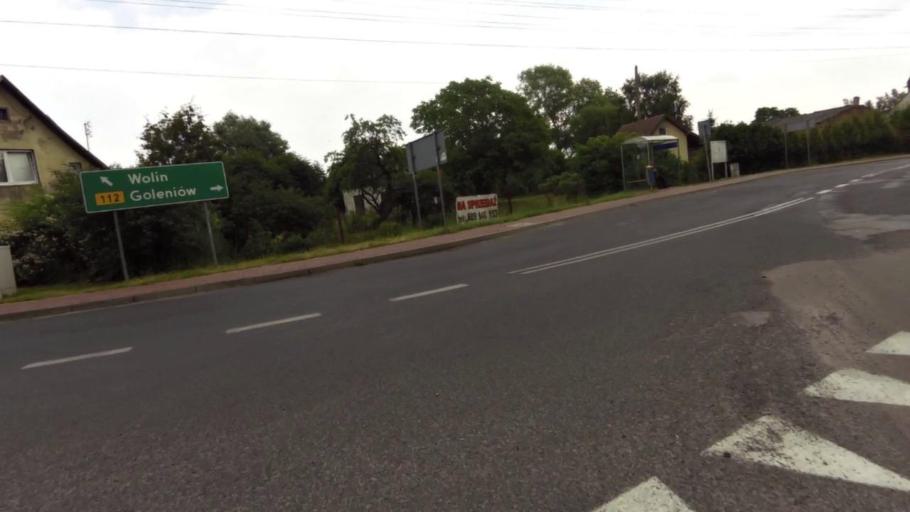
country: PL
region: West Pomeranian Voivodeship
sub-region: Powiat goleniowski
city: Stepnica
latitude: 53.6589
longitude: 14.6182
